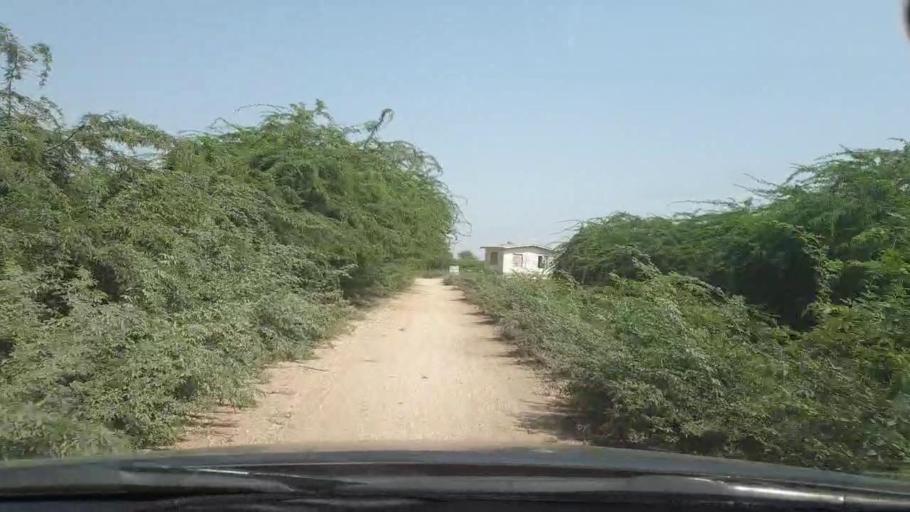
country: PK
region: Sindh
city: Naukot
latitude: 24.8088
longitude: 69.2671
